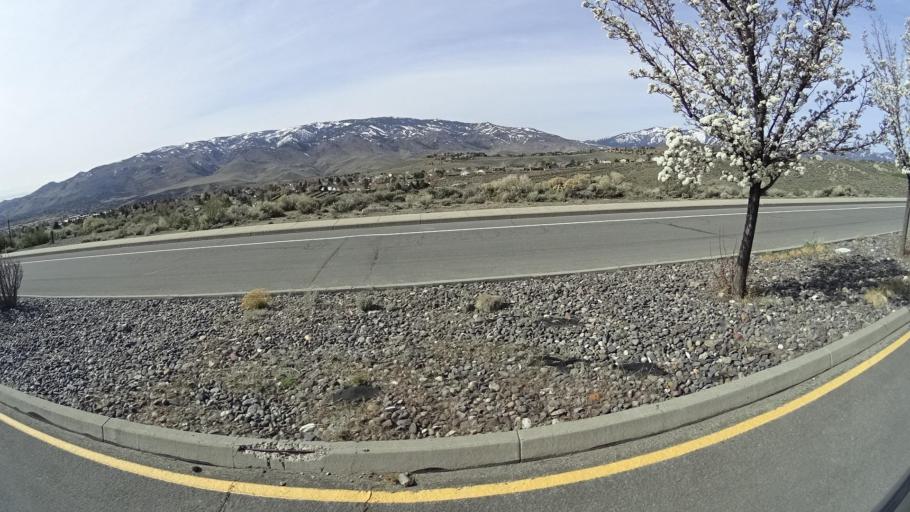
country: US
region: Nevada
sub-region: Washoe County
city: Mogul
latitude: 39.5315
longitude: -119.8975
